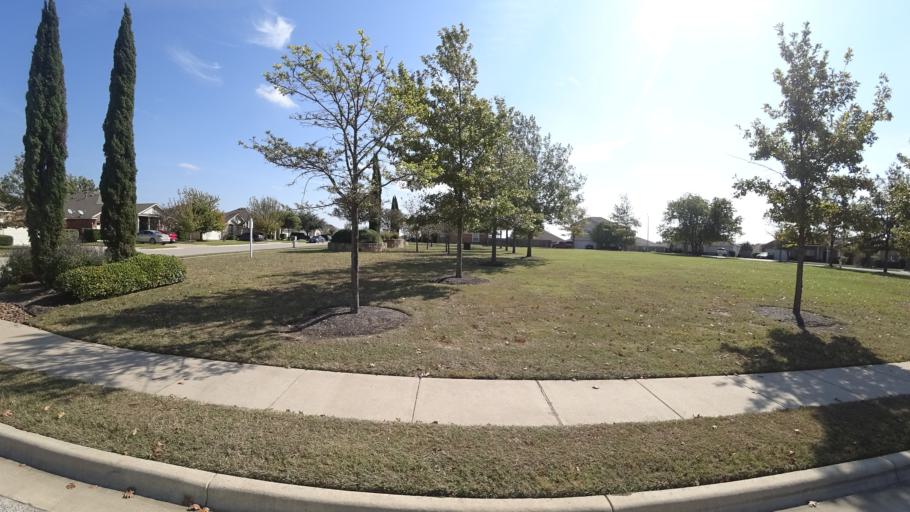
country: US
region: Texas
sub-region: Travis County
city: Pflugerville
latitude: 30.4203
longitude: -97.6339
